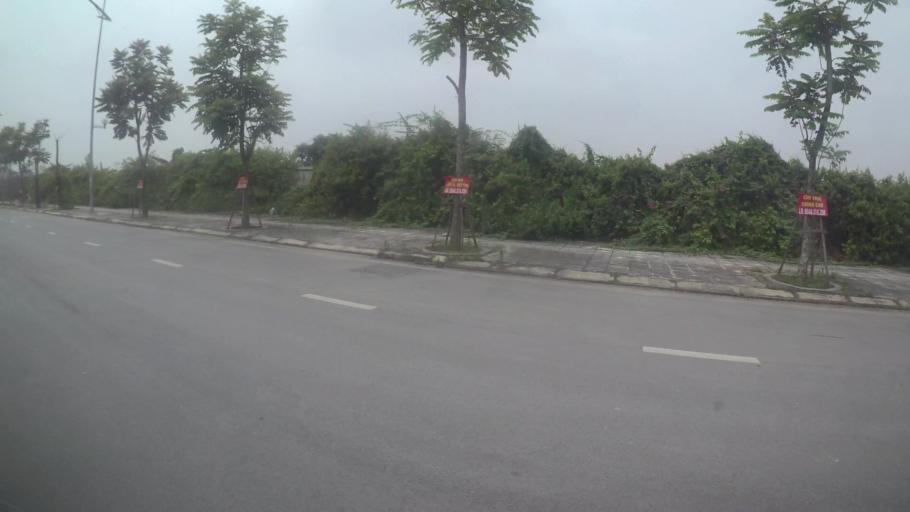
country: VN
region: Ha Noi
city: Cau Dien
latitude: 21.0295
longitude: 105.7443
